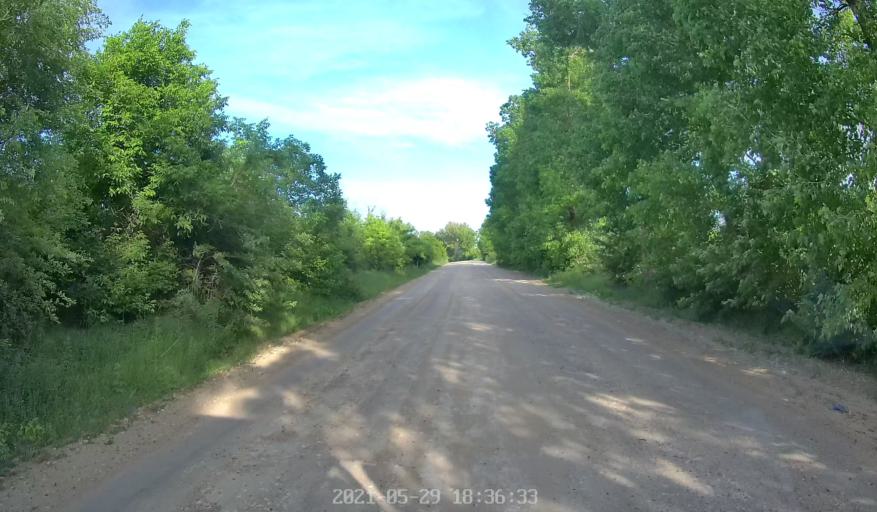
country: MD
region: Chisinau
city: Singera
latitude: 46.8063
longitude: 28.9252
